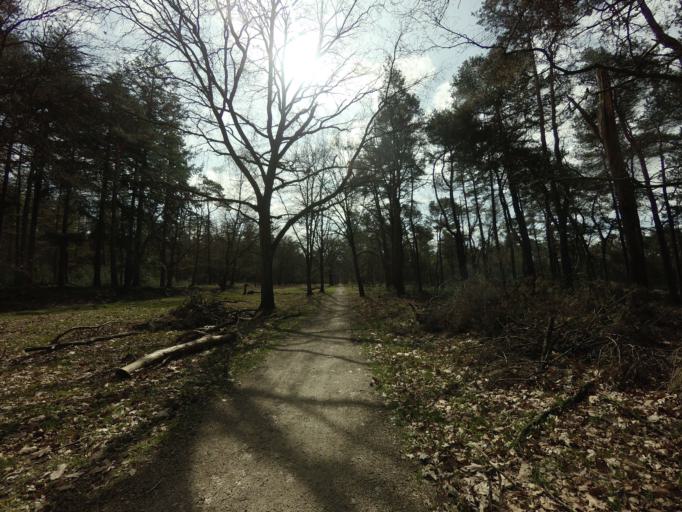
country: NL
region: North Holland
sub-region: Gemeente Hilversum
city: Hilversum
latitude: 52.1932
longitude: 5.1940
